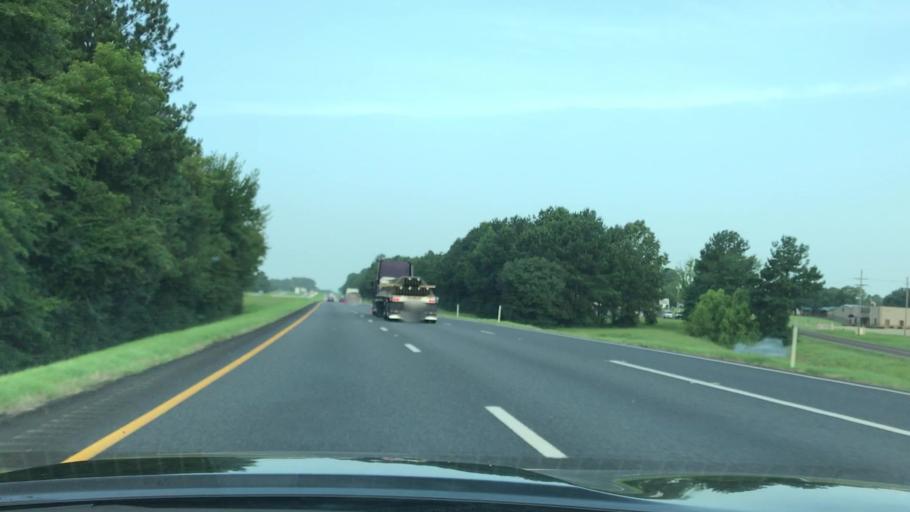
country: US
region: Texas
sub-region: Gregg County
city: Kilgore
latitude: 32.4351
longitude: -94.8316
